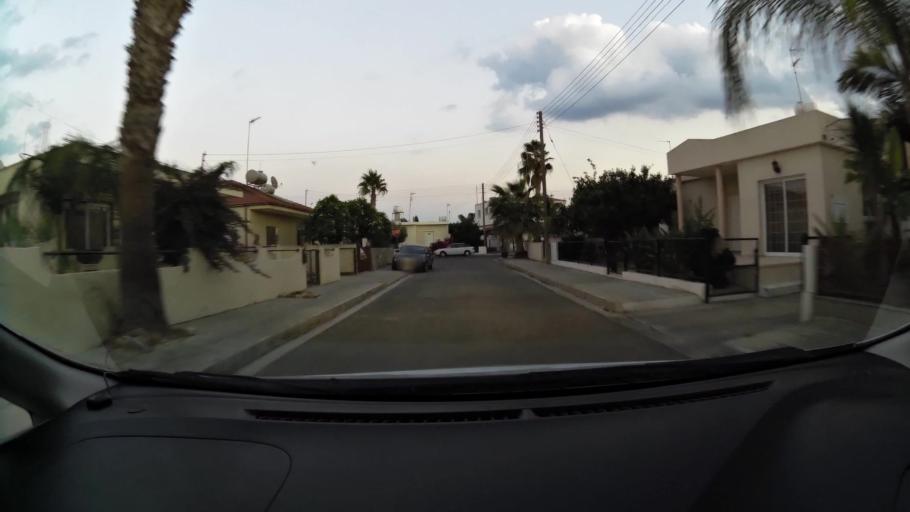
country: CY
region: Larnaka
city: Dhromolaxia
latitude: 34.8732
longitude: 33.5810
